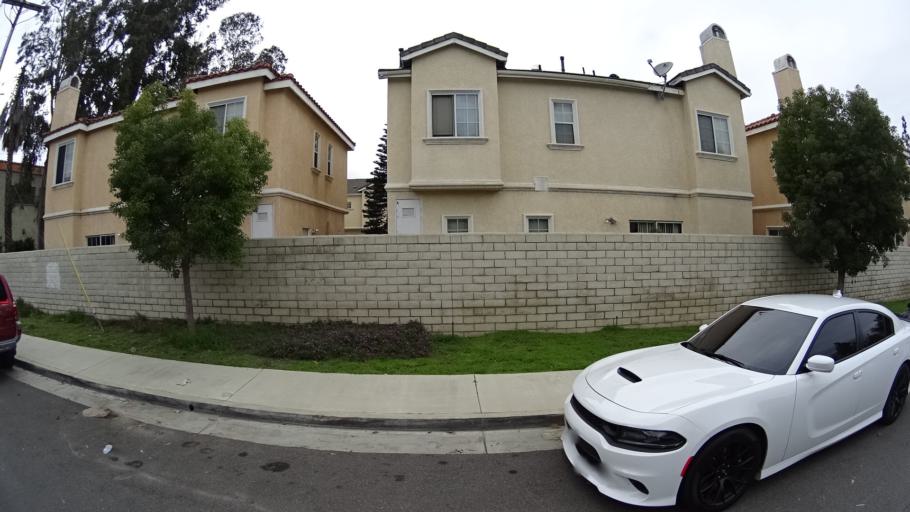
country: US
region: California
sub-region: Orange County
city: Yorba Linda
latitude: 33.8689
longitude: -117.8290
